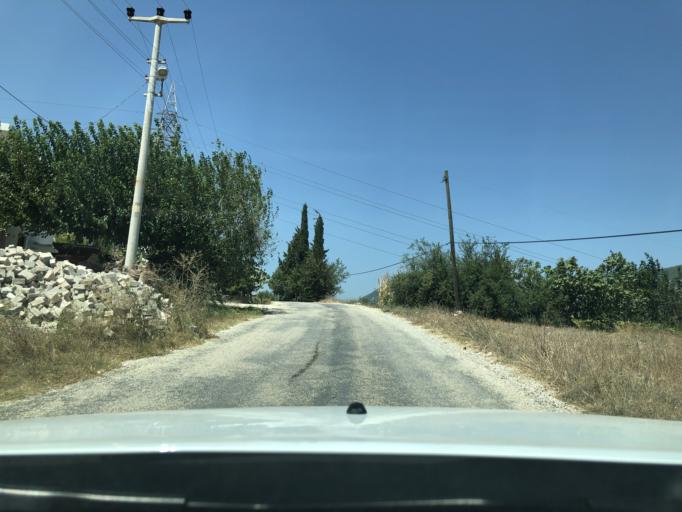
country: TR
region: Antalya
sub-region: Manavgat
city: Kizilagac
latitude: 36.8562
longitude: 31.5583
